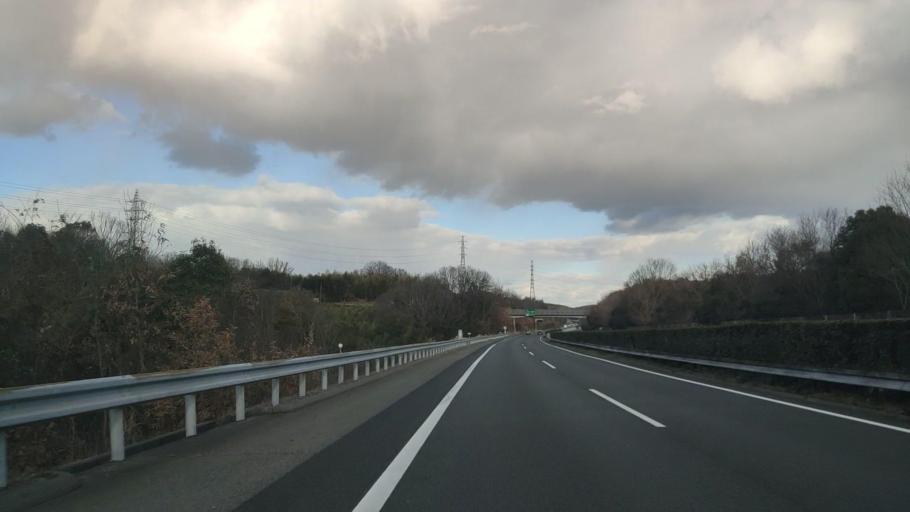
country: JP
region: Okayama
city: Kurashiki
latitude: 34.5806
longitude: 133.6782
